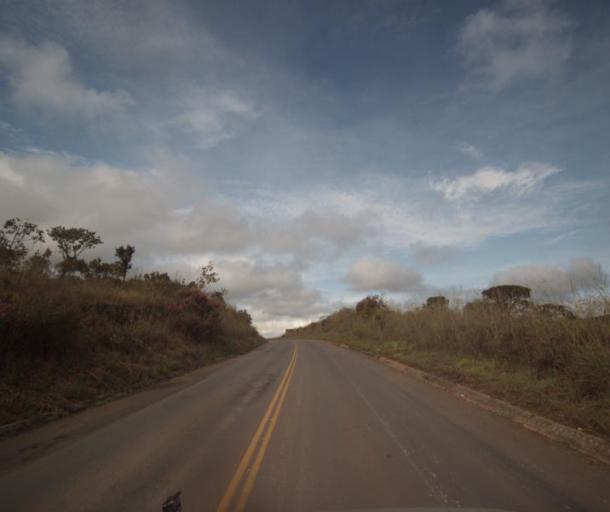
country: BR
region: Goias
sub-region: Pirenopolis
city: Pirenopolis
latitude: -15.8063
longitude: -48.7815
